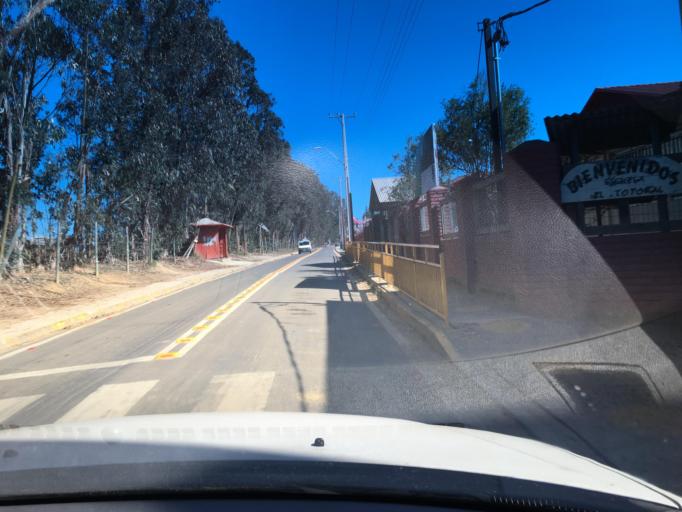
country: CL
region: Valparaiso
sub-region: San Antonio Province
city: El Tabo
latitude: -33.4204
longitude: -71.6254
